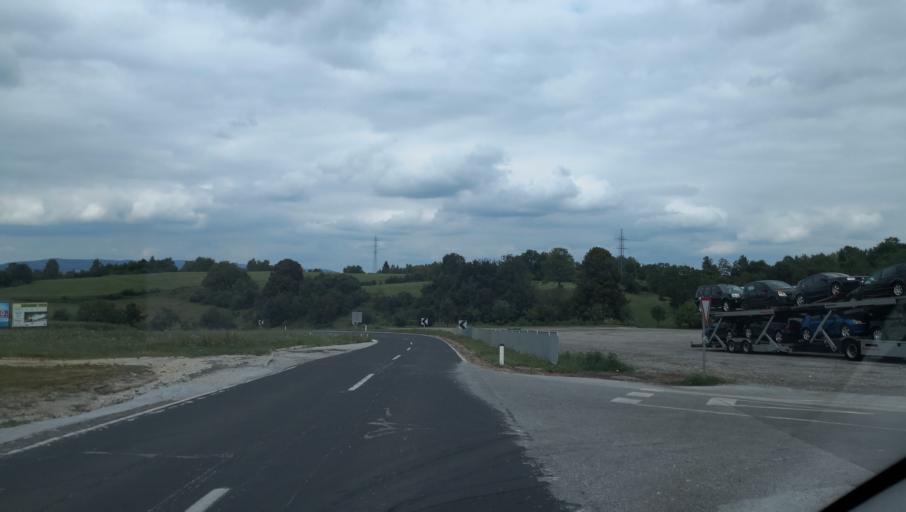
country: SI
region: Novo Mesto
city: Novo Mesto
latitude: 45.7605
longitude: 15.2004
